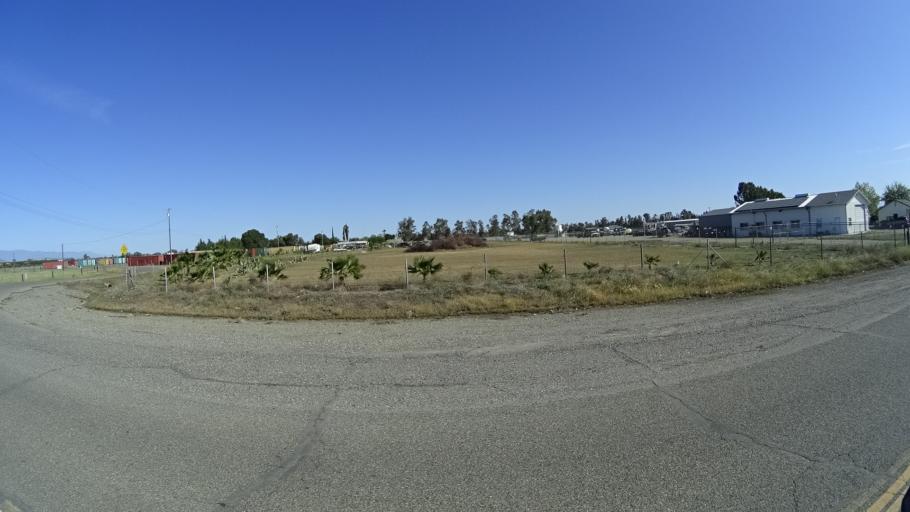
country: US
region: California
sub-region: Glenn County
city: Orland
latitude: 39.6968
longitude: -122.2033
